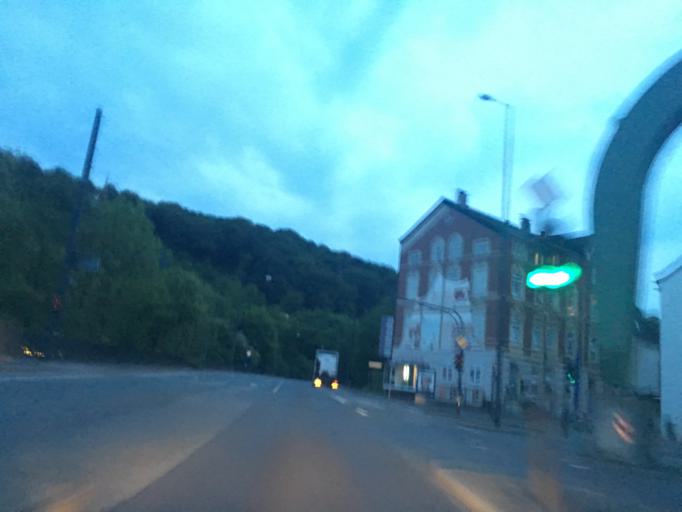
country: DE
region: North Rhine-Westphalia
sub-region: Regierungsbezirk Dusseldorf
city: Solingen
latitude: 51.2390
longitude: 7.1029
